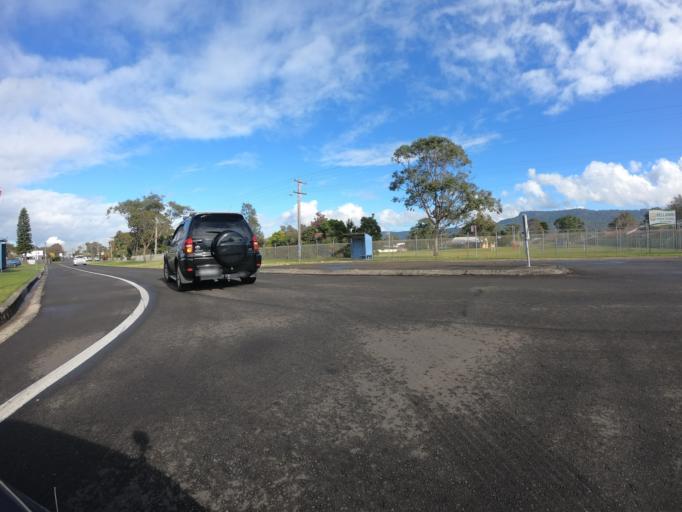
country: AU
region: New South Wales
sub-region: Wollongong
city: East Corrimal
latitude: -34.3714
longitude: 150.9160
